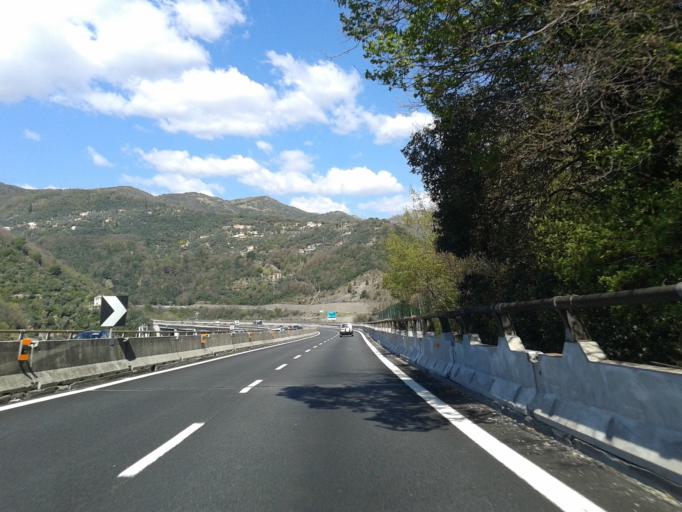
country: IT
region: Liguria
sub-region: Provincia di Genova
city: Avegno
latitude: 44.3711
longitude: 9.1536
